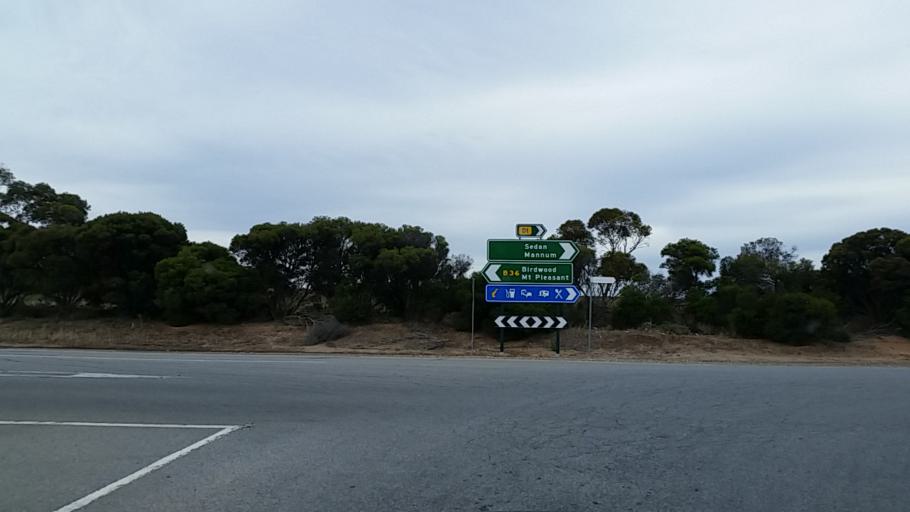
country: AU
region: South Australia
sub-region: Mid Murray
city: Mannum
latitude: -34.9040
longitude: 139.2817
